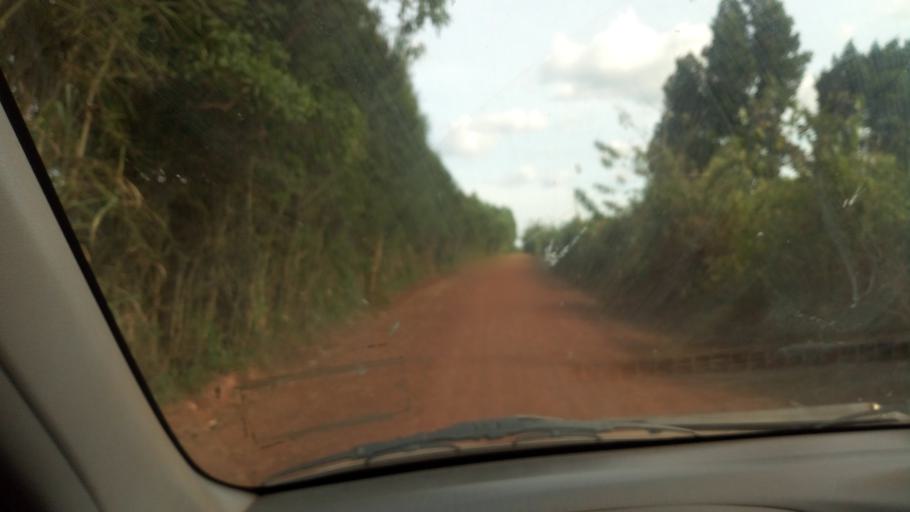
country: UG
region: Western Region
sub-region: Kiryandongo District
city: Kiryandongo
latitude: 1.8155
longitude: 31.9363
